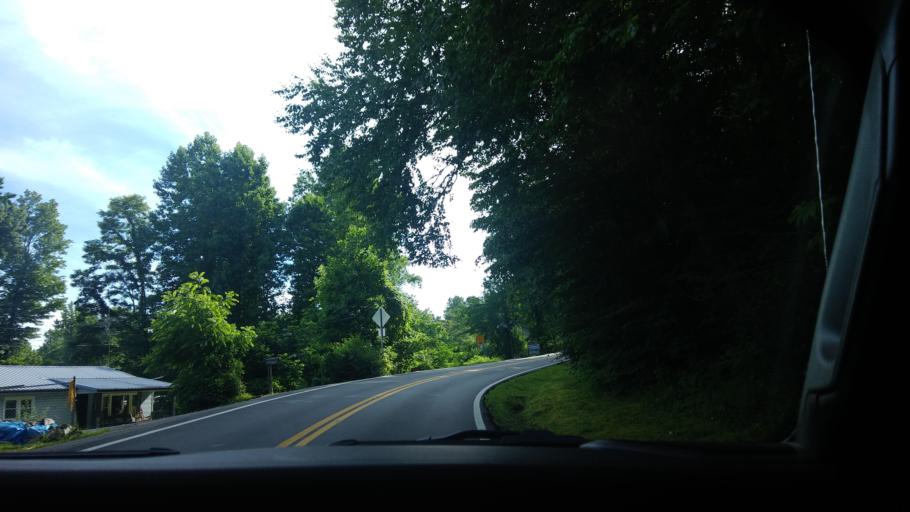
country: US
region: Tennessee
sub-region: Cocke County
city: Newport
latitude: 35.7852
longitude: -83.1930
